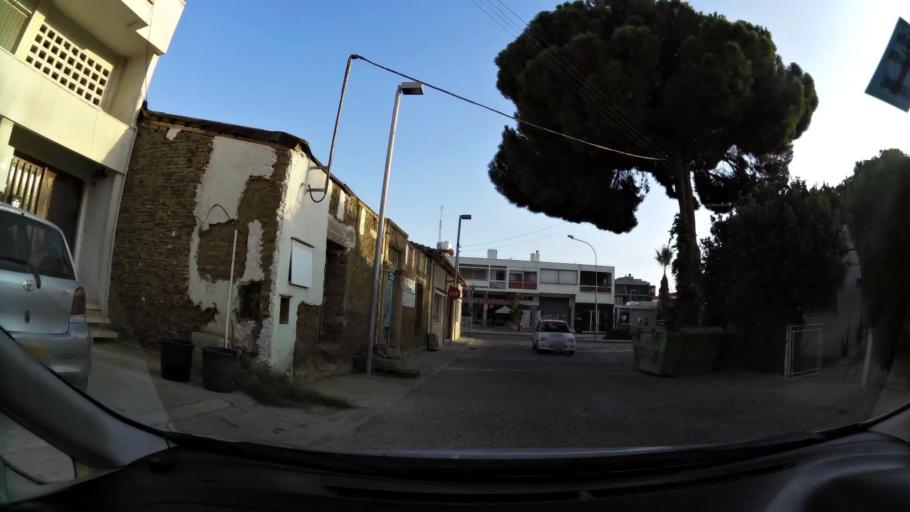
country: CY
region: Lefkosia
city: Nicosia
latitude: 35.1688
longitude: 33.3322
